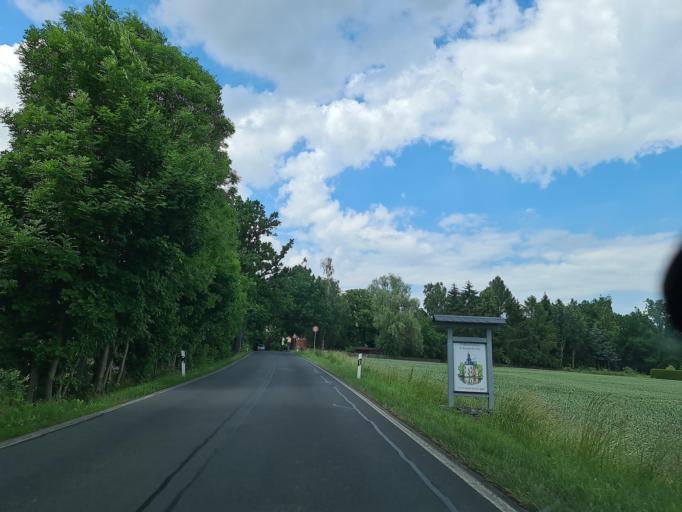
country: DE
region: Saxony
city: Syrau
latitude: 50.5196
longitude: 12.0918
